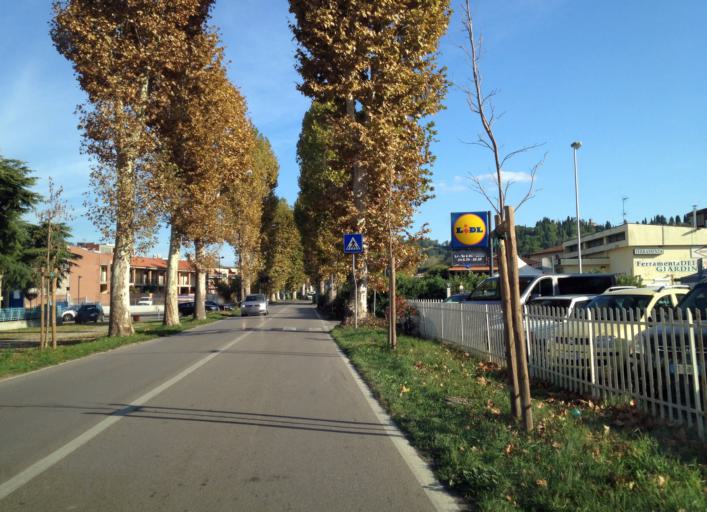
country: IT
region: Tuscany
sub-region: Provincia di Siena
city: Poggibonsi
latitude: 43.4687
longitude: 11.1364
